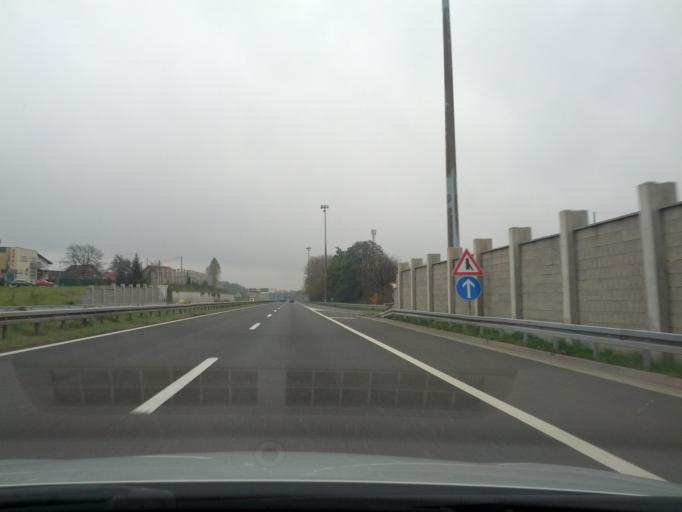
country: HR
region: Zagrebacka
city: Bestovje
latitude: 45.7975
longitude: 15.7856
